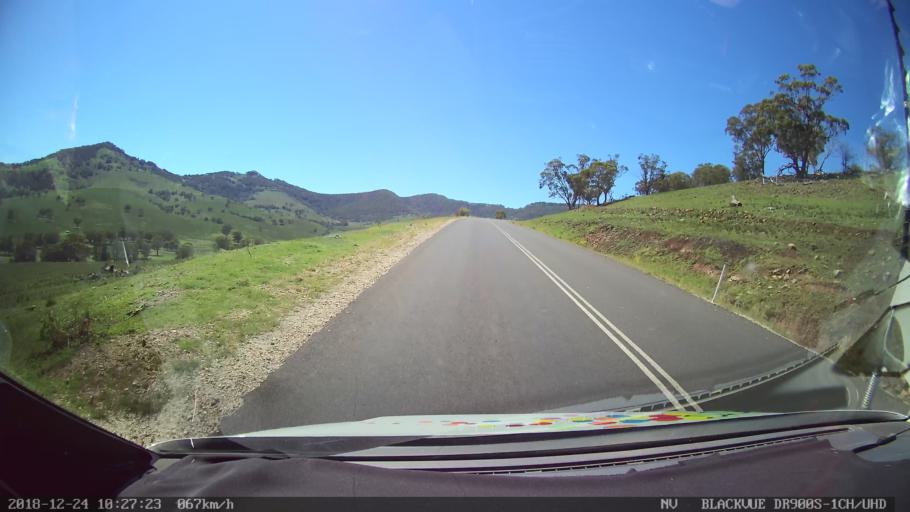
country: AU
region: New South Wales
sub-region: Liverpool Plains
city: Quirindi
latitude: -31.8171
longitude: 150.5324
